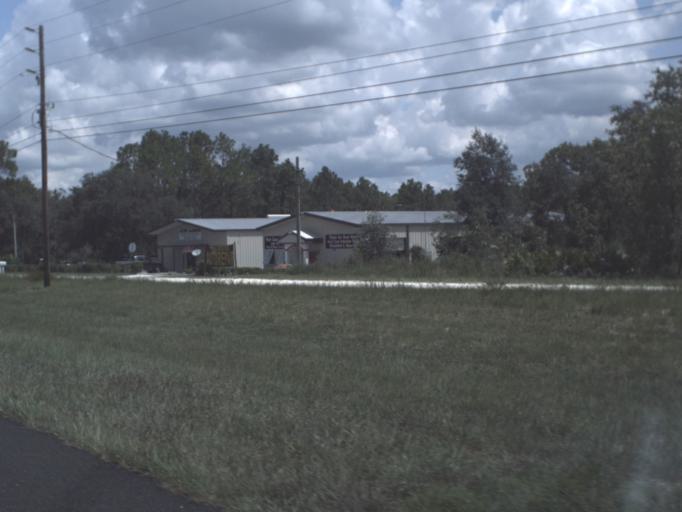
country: US
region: Florida
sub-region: Citrus County
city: Sugarmill Woods
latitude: 28.6759
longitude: -82.5522
